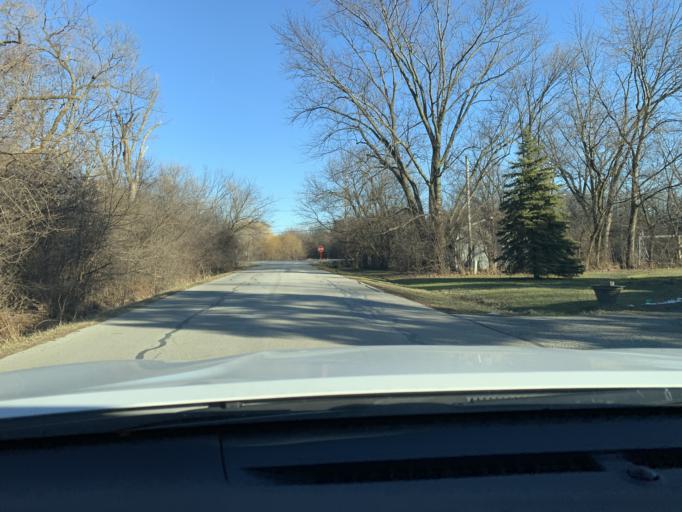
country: US
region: Illinois
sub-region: Cook County
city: Lemont
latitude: 41.7075
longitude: -88.0078
